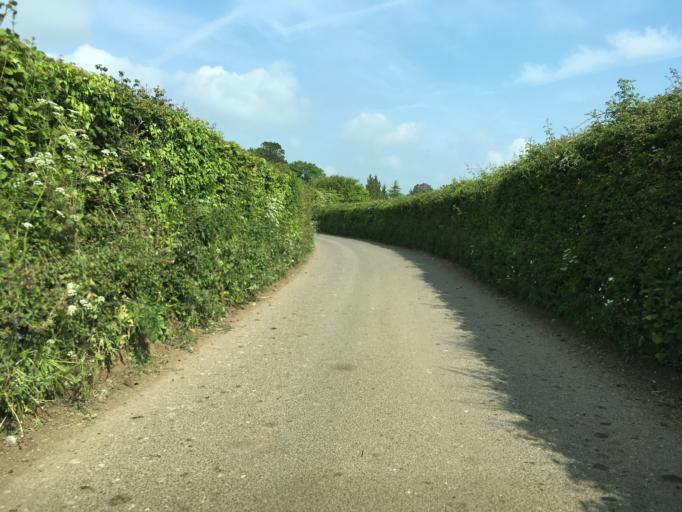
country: GB
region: England
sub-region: North Somerset
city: Dundry
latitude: 51.3974
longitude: -2.6341
